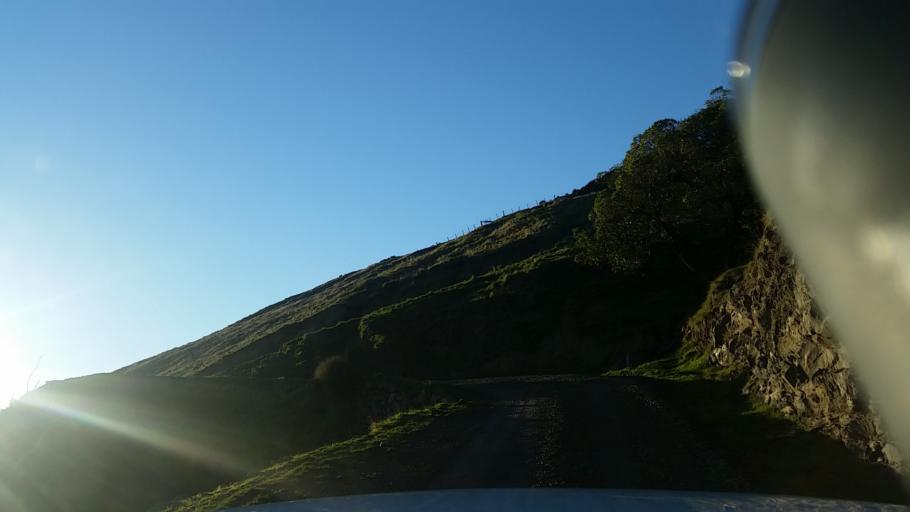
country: NZ
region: Canterbury
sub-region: Christchurch City
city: Christchurch
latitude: -43.7239
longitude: 173.1005
